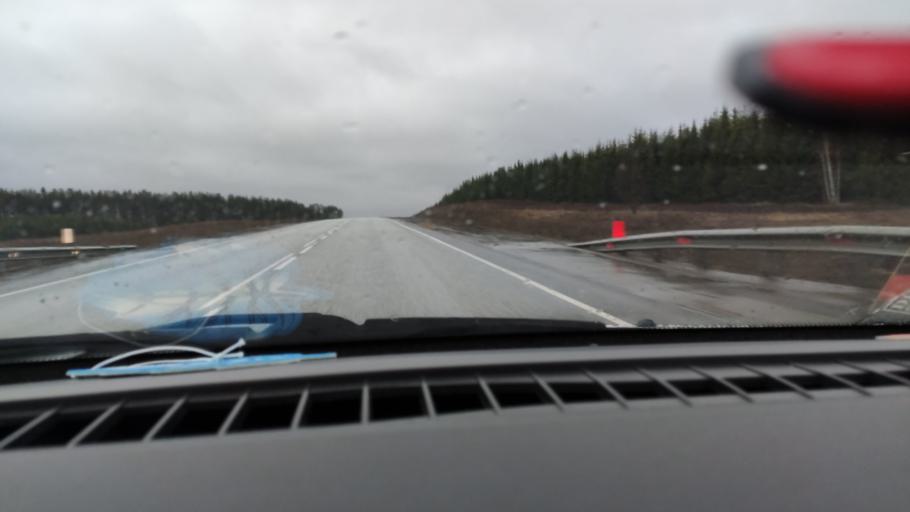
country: RU
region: Udmurtiya
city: Alnashi
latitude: 56.0543
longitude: 52.3925
